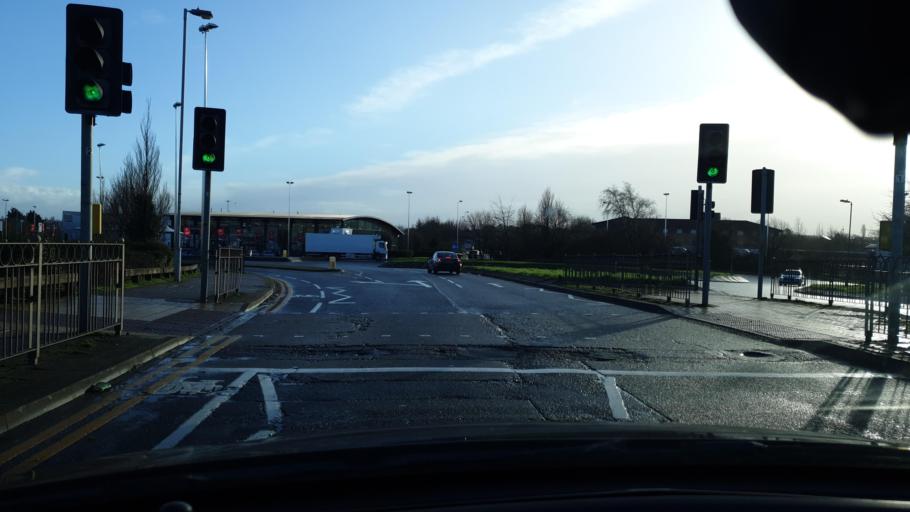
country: GB
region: England
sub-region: City and Borough of Birmingham
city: Birmingham
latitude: 52.5038
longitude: -1.8583
